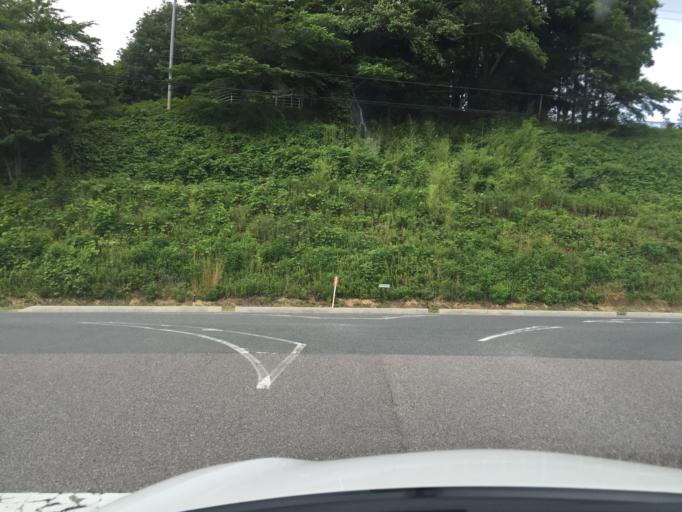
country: JP
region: Fukushima
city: Miharu
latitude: 37.3957
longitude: 140.4856
